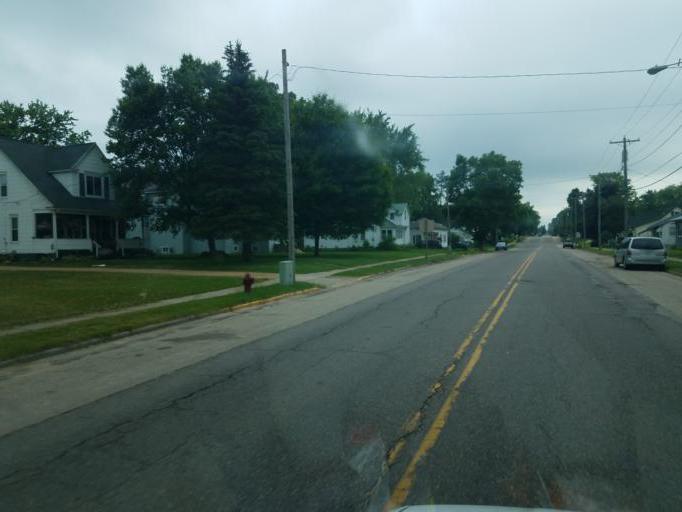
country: US
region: Wisconsin
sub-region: Juneau County
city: Elroy
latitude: 43.7464
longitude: -90.2732
